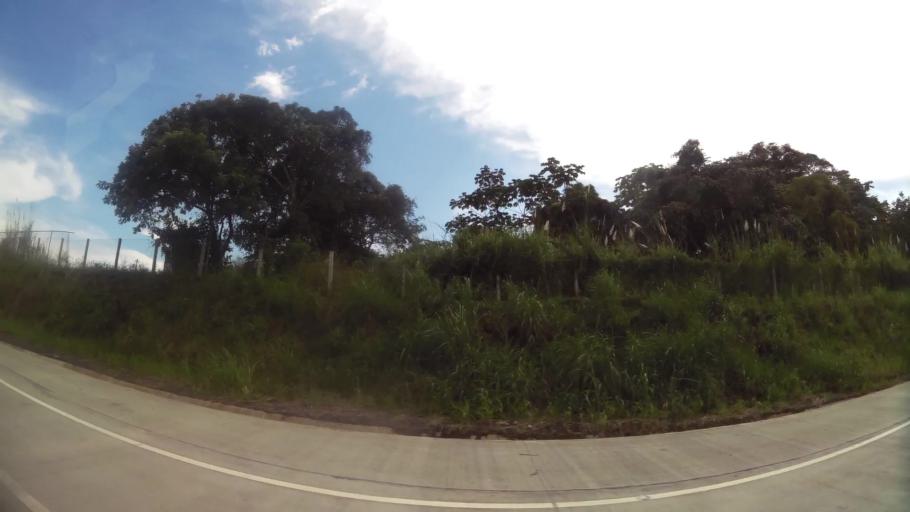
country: PA
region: Panama
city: San Miguelito
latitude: 9.0793
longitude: -79.4581
